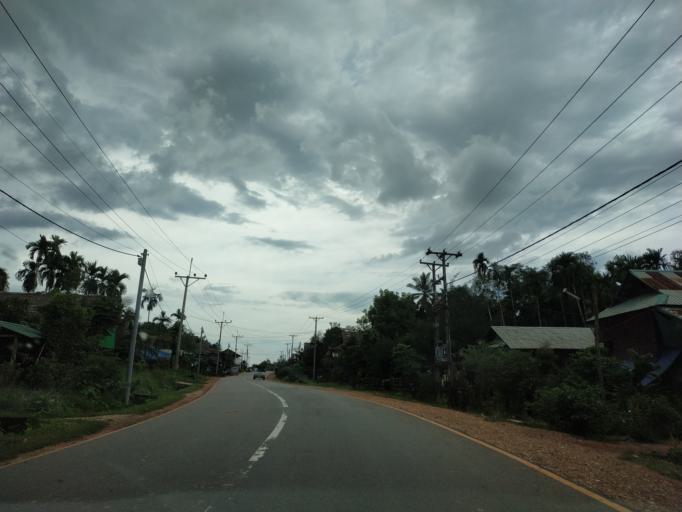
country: MM
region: Tanintharyi
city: Dawei
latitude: 13.9123
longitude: 98.2504
